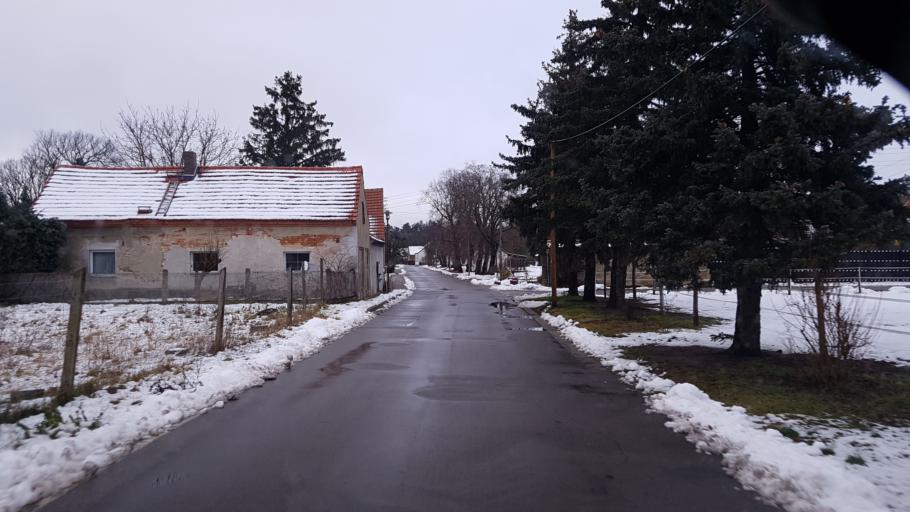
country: DE
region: Brandenburg
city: Luckau
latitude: 51.8600
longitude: 13.8136
